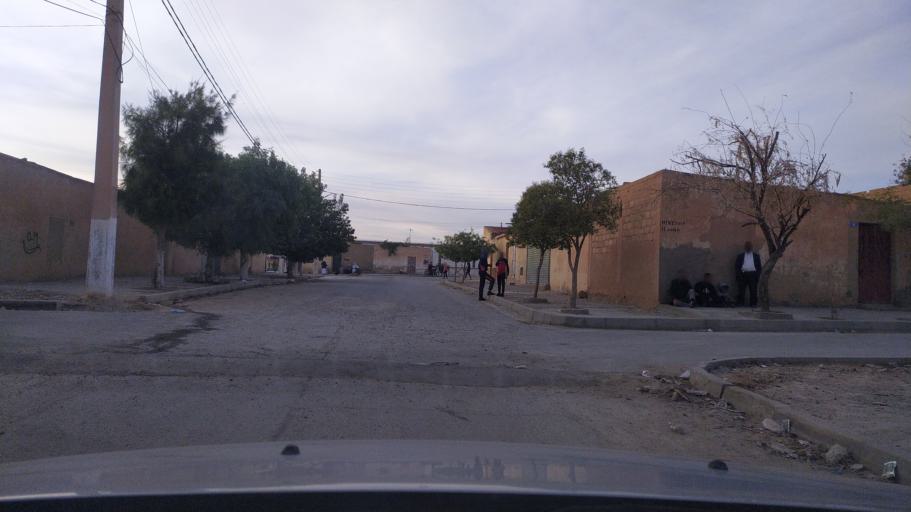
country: DZ
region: Tiaret
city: Frenda
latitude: 34.9005
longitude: 1.2368
